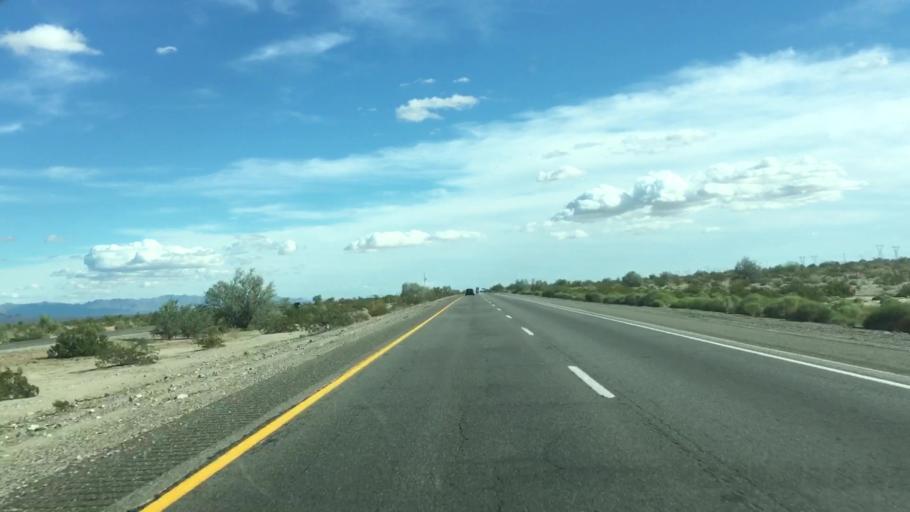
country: US
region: California
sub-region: Imperial County
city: Niland
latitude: 33.6961
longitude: -115.2903
